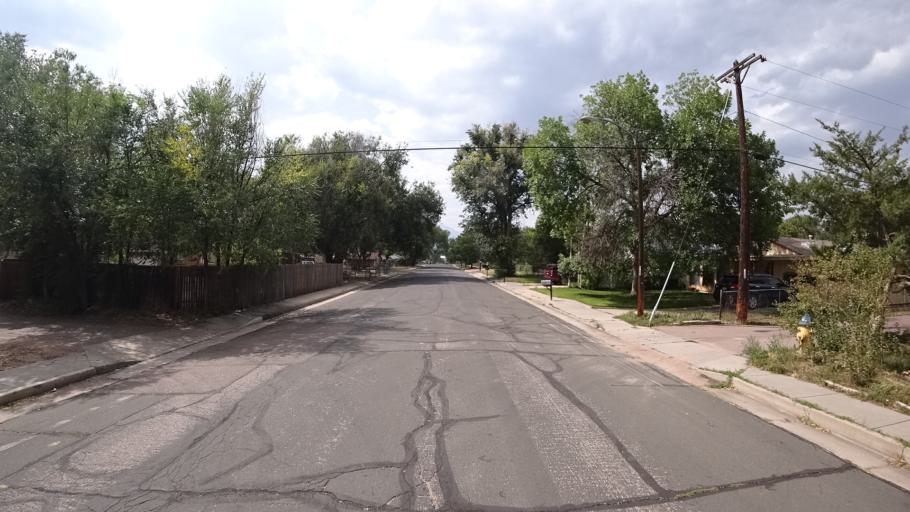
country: US
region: Colorado
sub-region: El Paso County
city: Colorado Springs
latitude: 38.8423
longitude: -104.7878
